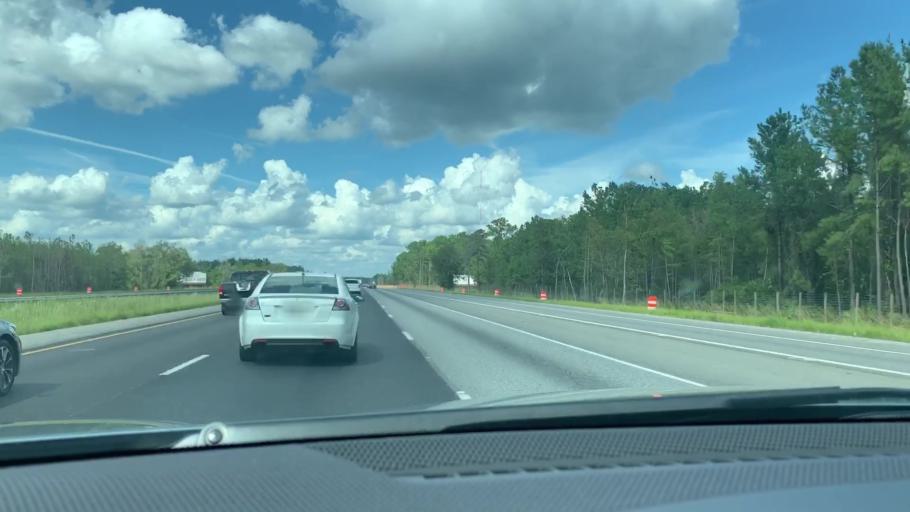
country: US
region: Georgia
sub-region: Camden County
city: Kingsland
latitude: 30.8525
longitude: -81.6748
